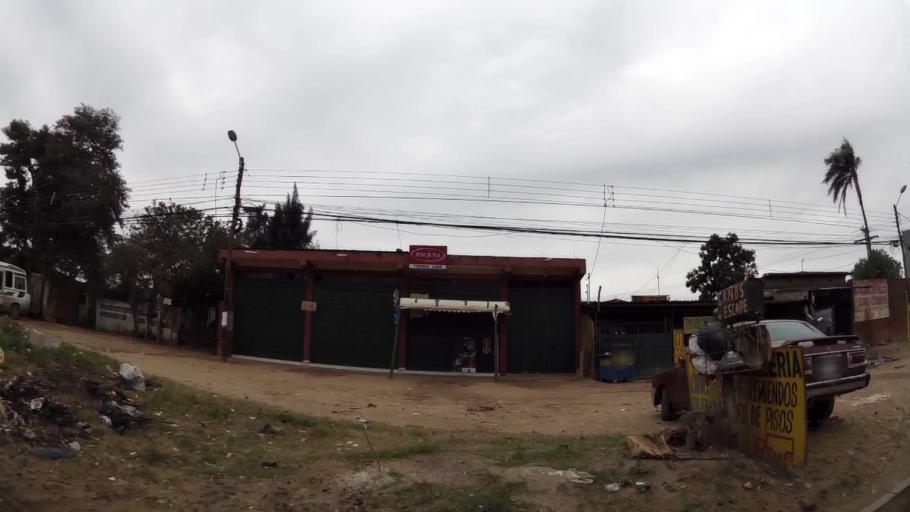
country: BO
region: Santa Cruz
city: Santa Cruz de la Sierra
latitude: -17.8241
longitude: -63.2068
